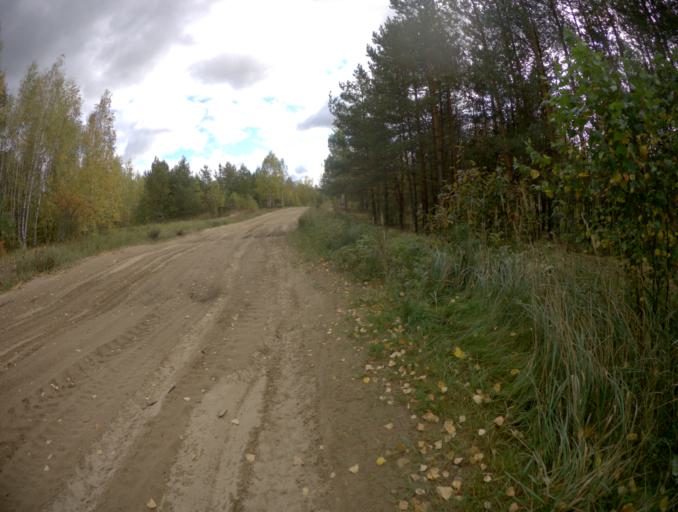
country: RU
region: Vladimir
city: Petushki
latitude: 55.8853
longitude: 39.5048
